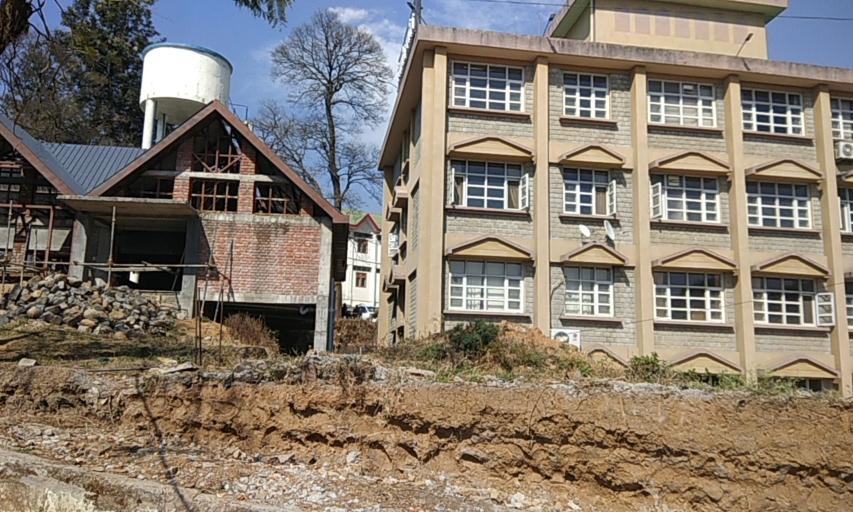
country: IN
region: Himachal Pradesh
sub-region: Kangra
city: Dharmsala
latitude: 32.2076
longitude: 76.3226
